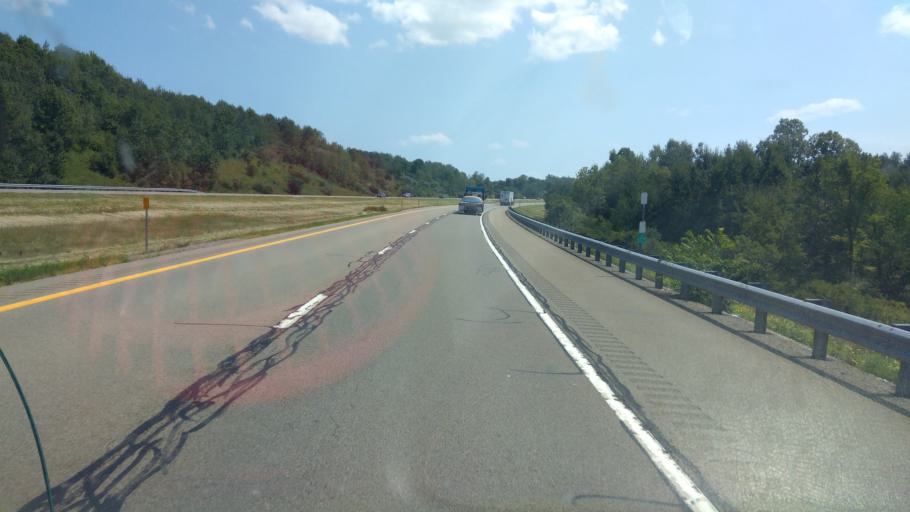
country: US
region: New York
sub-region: Steuben County
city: Canisteo
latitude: 42.3796
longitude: -77.5314
